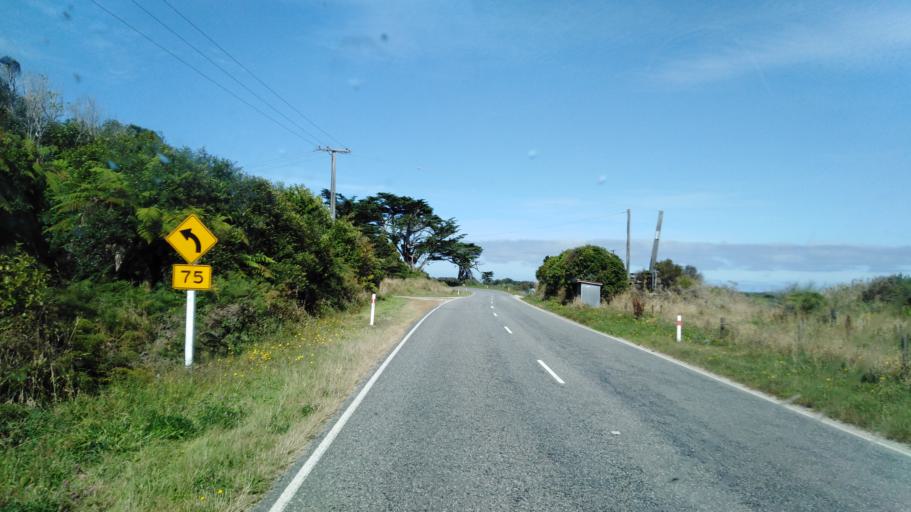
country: NZ
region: West Coast
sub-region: Buller District
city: Westport
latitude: -41.2910
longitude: 172.0959
